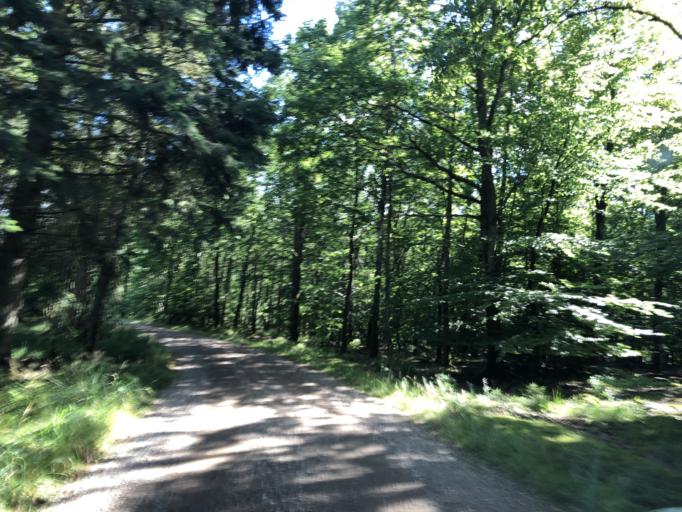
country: DK
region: Central Jutland
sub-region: Holstebro Kommune
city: Ulfborg
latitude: 56.2518
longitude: 8.4681
